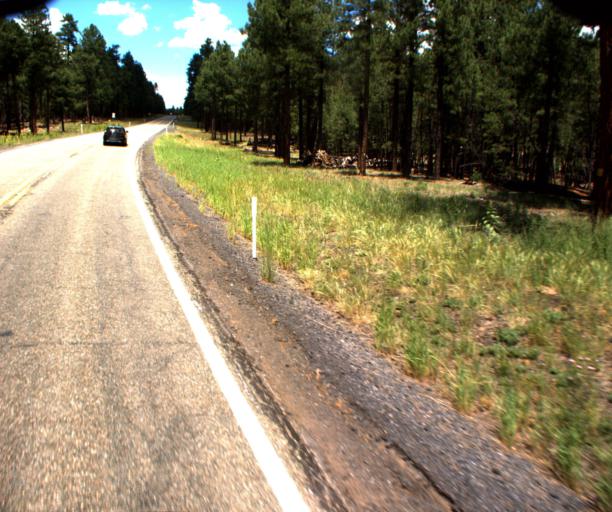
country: US
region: Arizona
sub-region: Coconino County
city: Flagstaff
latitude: 35.2708
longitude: -111.7429
